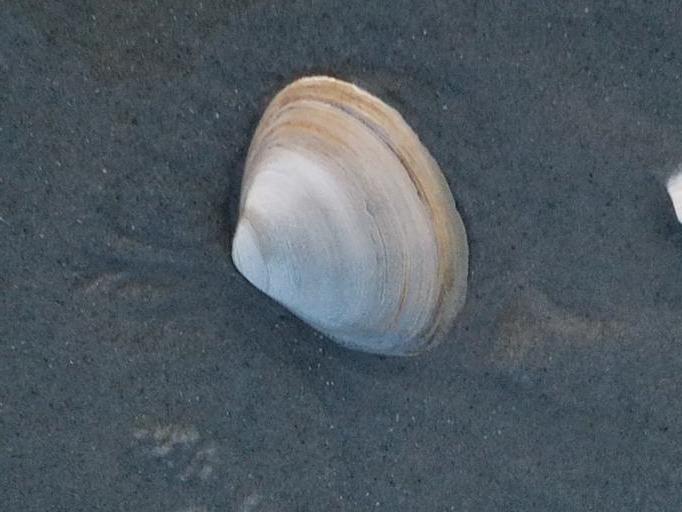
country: US
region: New York
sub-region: Suffolk County
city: West Bay Shore
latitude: 40.6220
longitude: -73.2795
